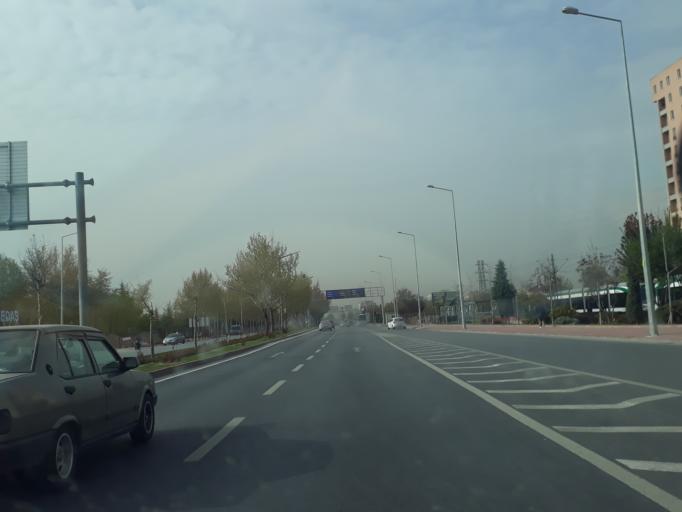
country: TR
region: Konya
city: Selcuklu
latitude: 37.9549
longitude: 32.5135
